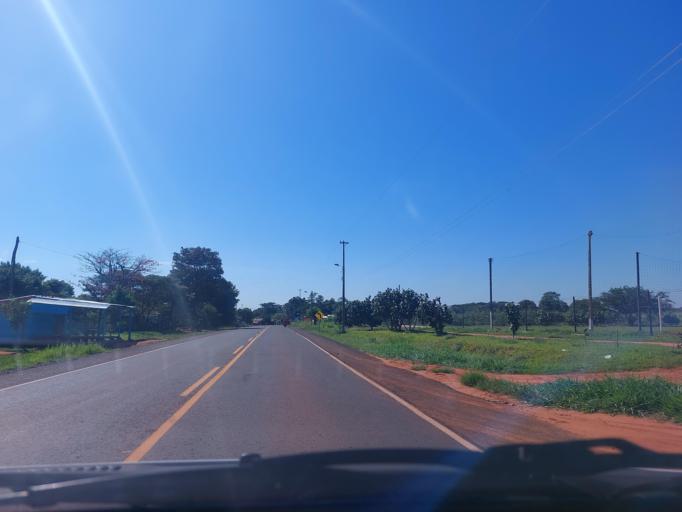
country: PY
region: San Pedro
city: Guayaybi
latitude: -24.3158
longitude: -56.1631
